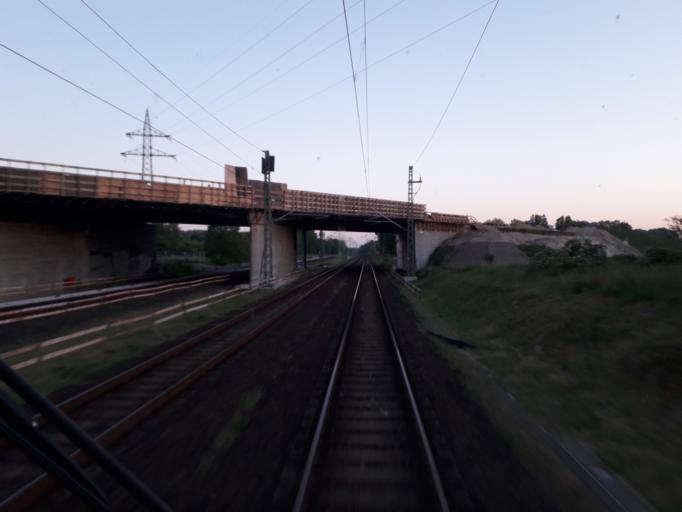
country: DE
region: Berlin
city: Buchholz
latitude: 52.6303
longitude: 13.4281
